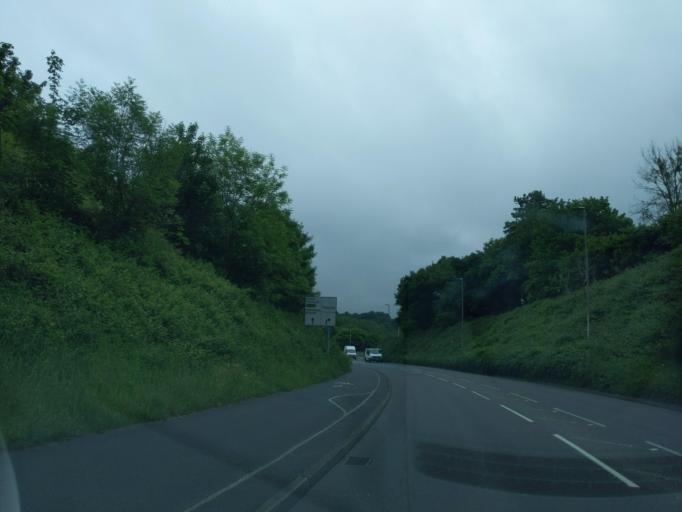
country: GB
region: England
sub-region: Devon
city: Plympton
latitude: 50.3831
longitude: -4.0256
